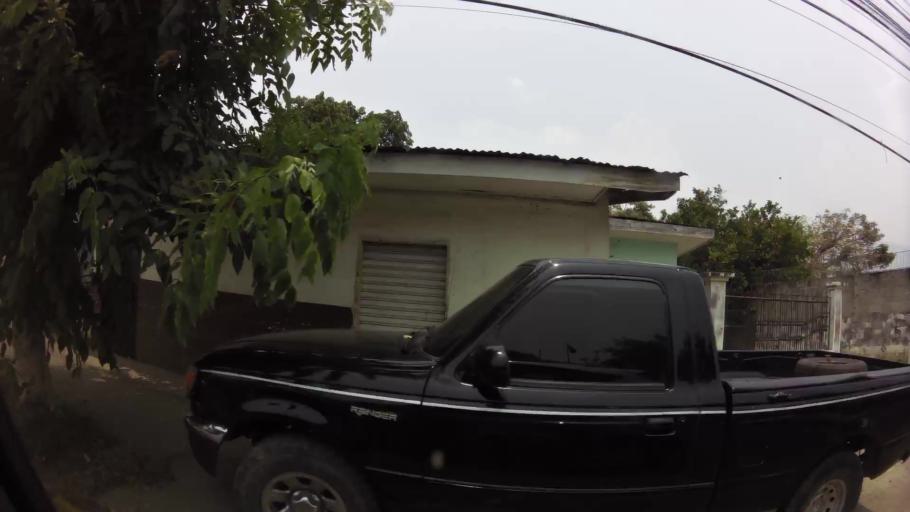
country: HN
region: Yoro
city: El Progreso
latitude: 15.3946
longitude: -87.8080
